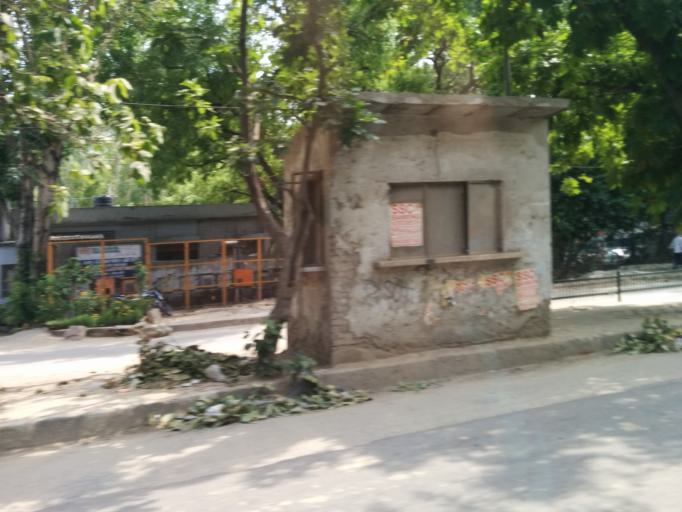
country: IN
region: NCT
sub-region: New Delhi
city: New Delhi
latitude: 28.5463
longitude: 77.1957
